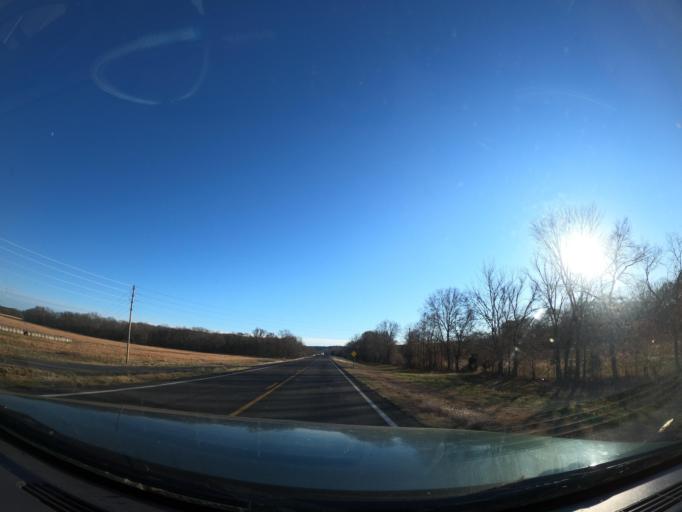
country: US
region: Oklahoma
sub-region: Latimer County
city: Wilburton
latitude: 34.9448
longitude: -95.3413
